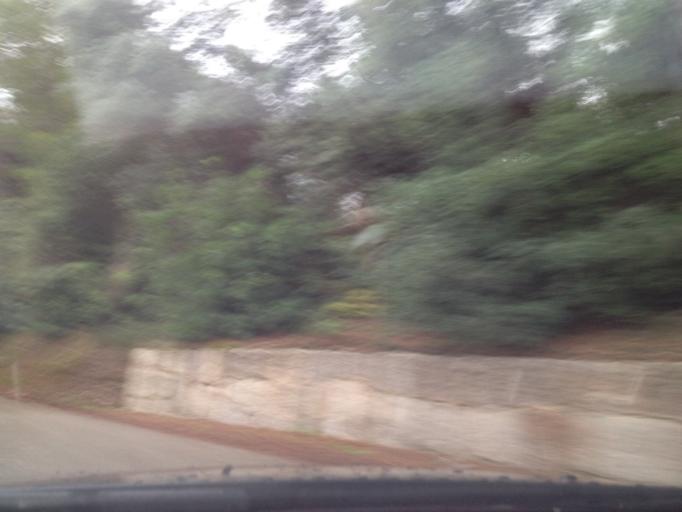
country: ES
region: Balearic Islands
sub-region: Illes Balears
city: Soller
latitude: 39.7744
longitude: 2.6837
